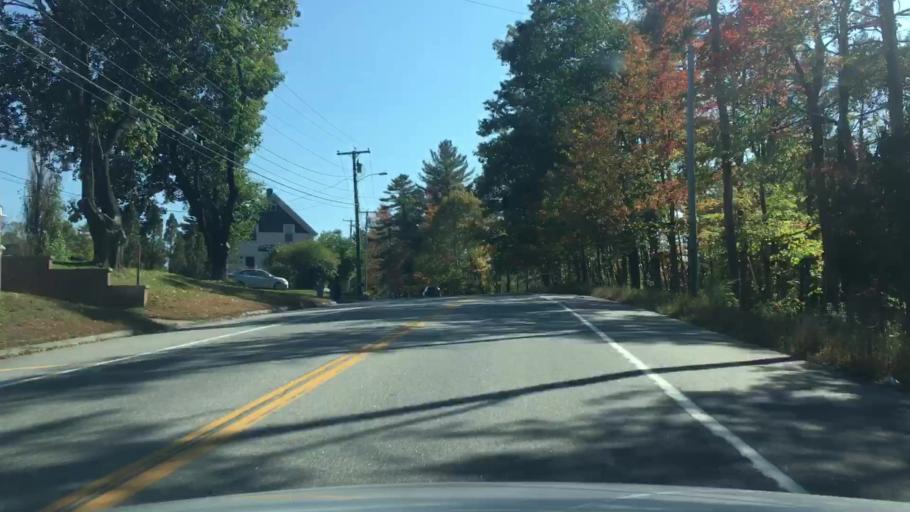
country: US
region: Maine
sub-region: Androscoggin County
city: Lisbon Falls
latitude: 43.9900
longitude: -70.0461
